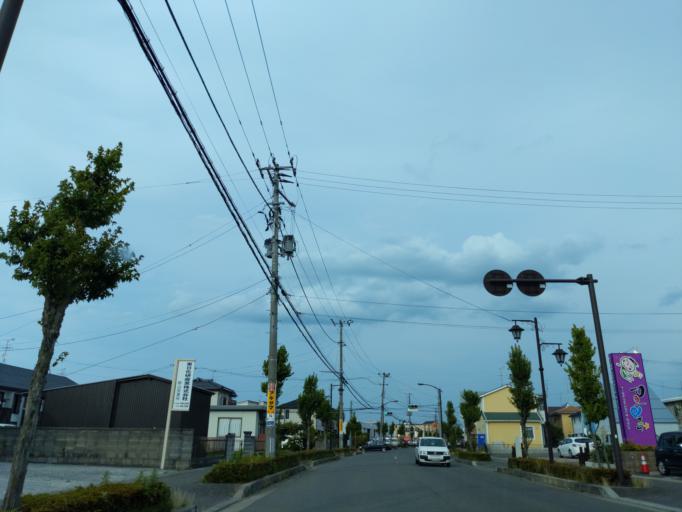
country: JP
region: Fukushima
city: Koriyama
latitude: 37.4294
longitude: 140.3720
